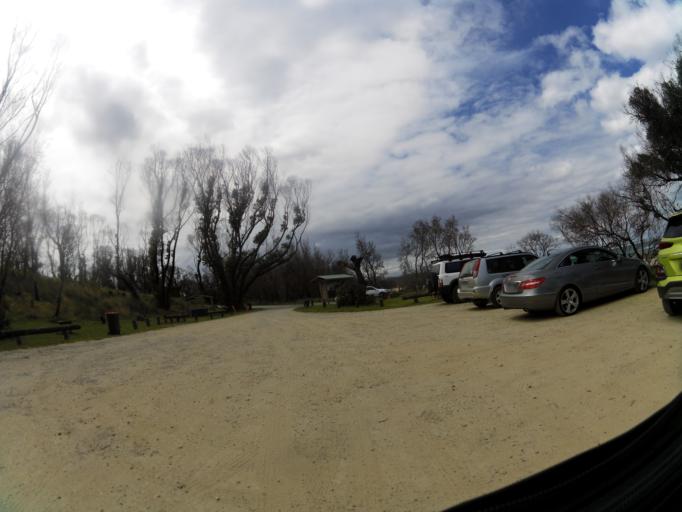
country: AU
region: Victoria
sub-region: East Gippsland
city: Lakes Entrance
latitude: -37.8026
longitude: 148.7411
